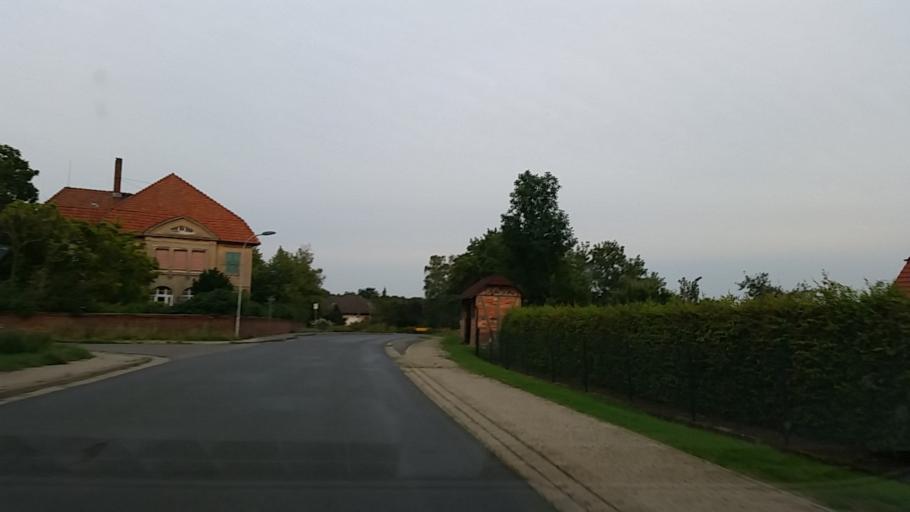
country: DE
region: Lower Saxony
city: Vordorf
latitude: 52.3557
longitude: 10.4932
